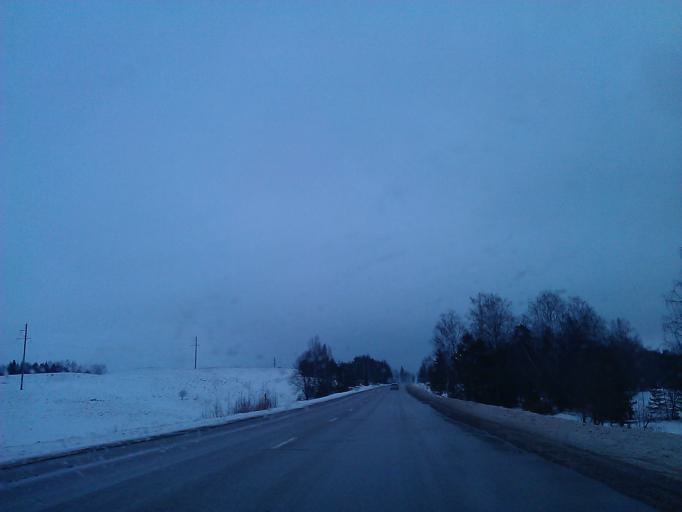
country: LV
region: Amatas Novads
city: Drabesi
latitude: 57.2625
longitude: 25.2691
